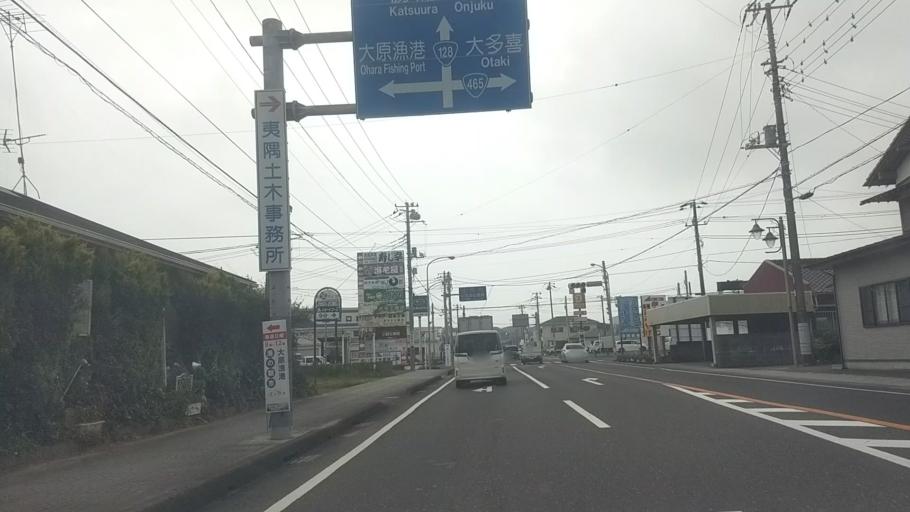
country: JP
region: Chiba
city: Ohara
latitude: 35.2549
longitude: 140.3951
